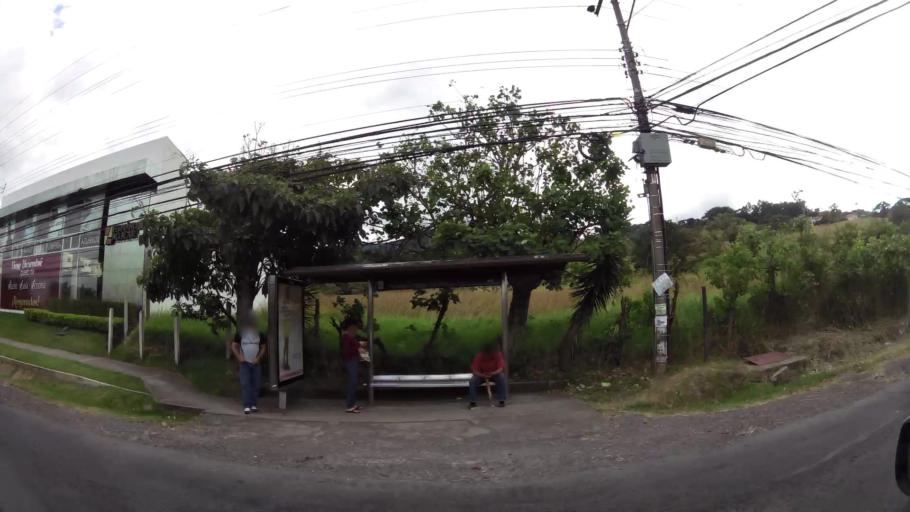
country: CR
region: San Jose
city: San Rafael
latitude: 9.9341
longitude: -84.1545
